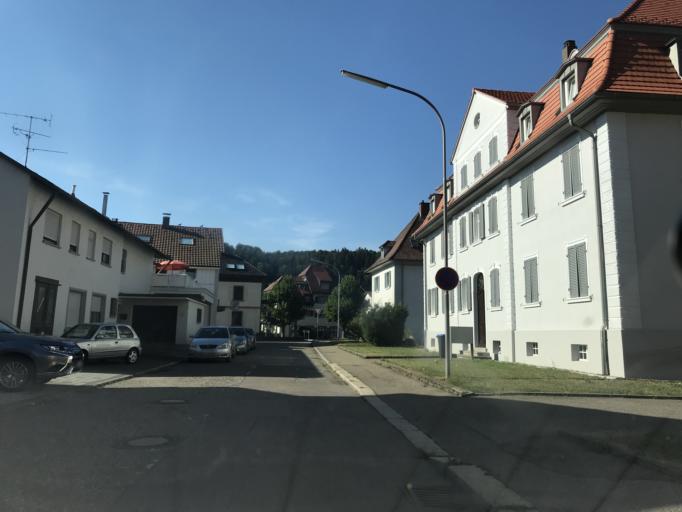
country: DE
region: Baden-Wuerttemberg
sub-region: Freiburg Region
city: Schopfheim
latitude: 47.6484
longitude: 7.8282
